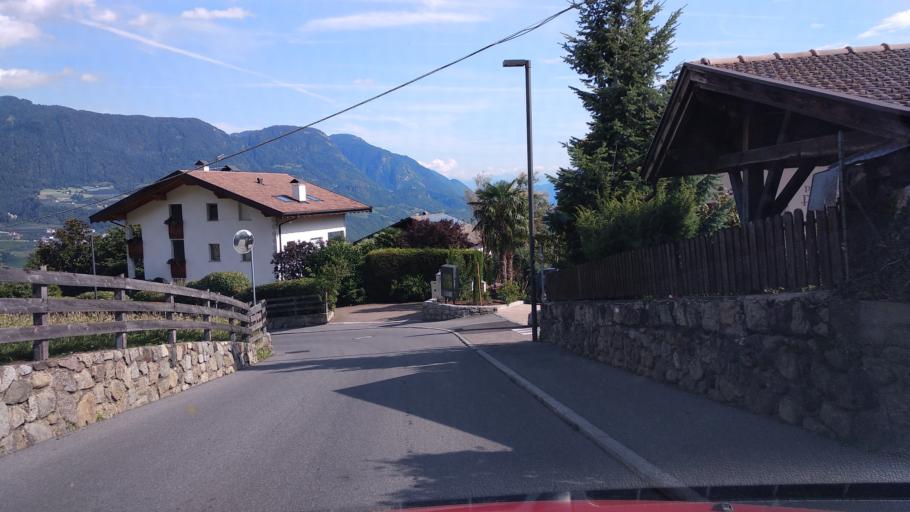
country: IT
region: Trentino-Alto Adige
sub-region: Bolzano
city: Tirolo
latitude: 46.6959
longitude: 11.1534
